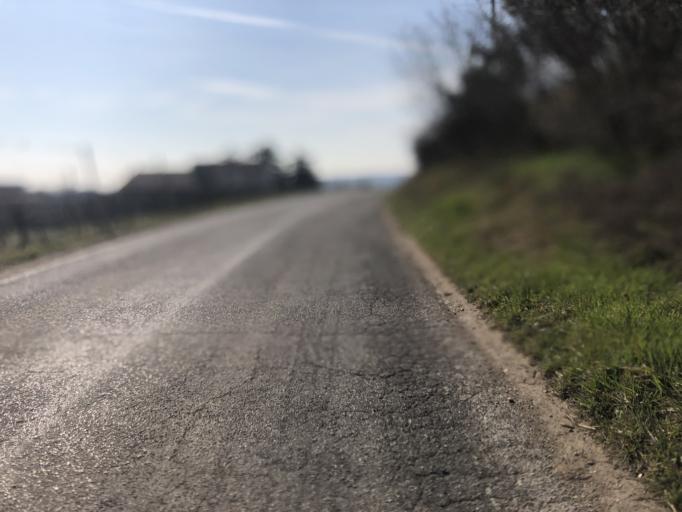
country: IT
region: Veneto
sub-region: Provincia di Verona
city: San Giorgio in Salici
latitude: 45.4028
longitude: 10.7774
